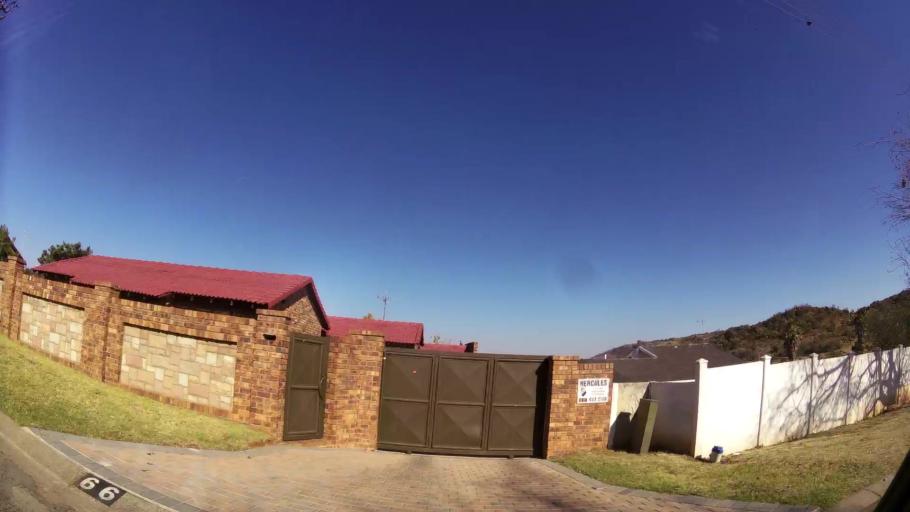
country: ZA
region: Gauteng
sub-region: City of Johannesburg Metropolitan Municipality
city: Johannesburg
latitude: -26.2775
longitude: 28.0331
